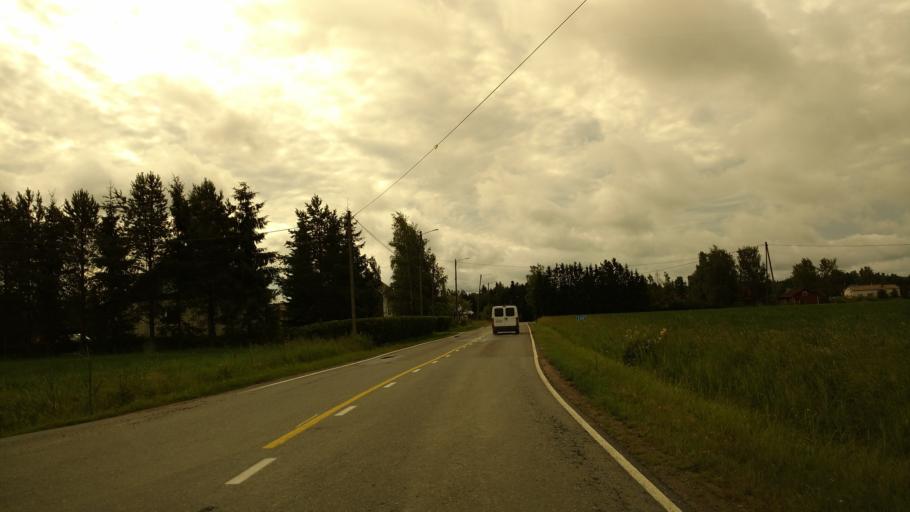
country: FI
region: Varsinais-Suomi
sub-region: Salo
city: Kuusjoki
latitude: 60.5397
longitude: 23.1669
